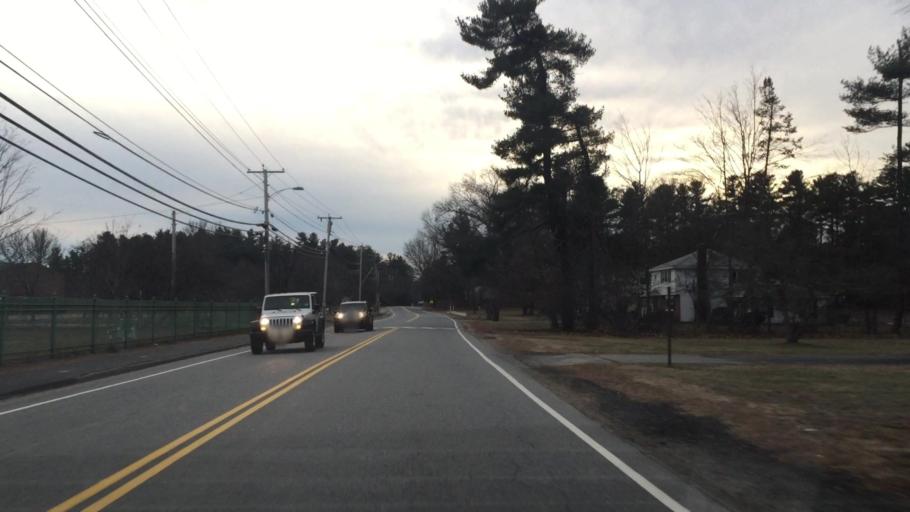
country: US
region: New Hampshire
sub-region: Hillsborough County
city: Pelham
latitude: 42.7288
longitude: -71.3270
